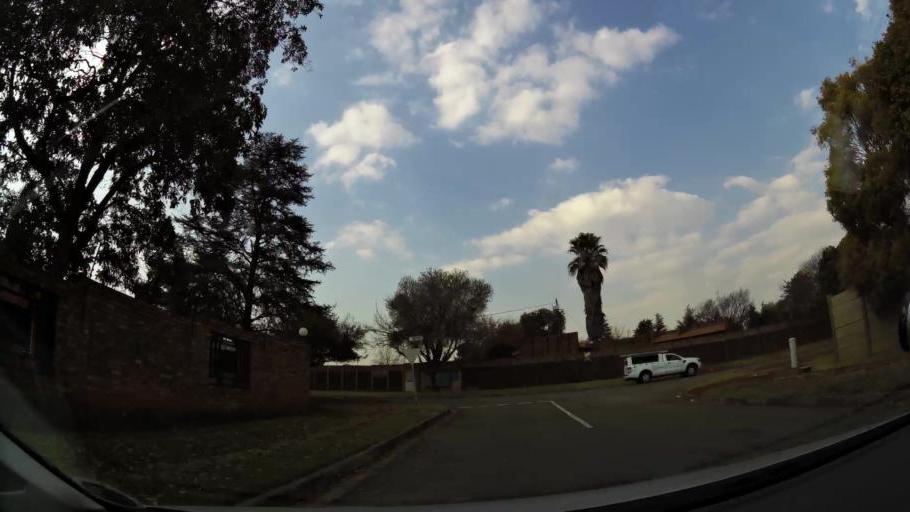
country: ZA
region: Gauteng
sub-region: City of Johannesburg Metropolitan Municipality
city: Modderfontein
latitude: -26.1387
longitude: 28.1918
